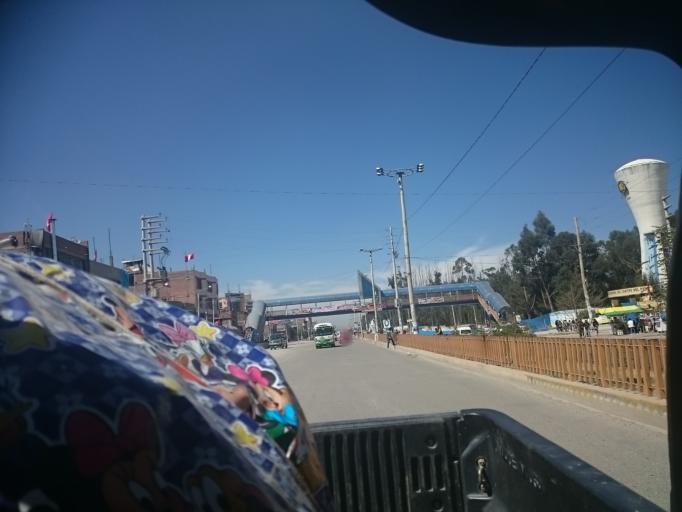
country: PE
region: Junin
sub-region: Provincia de Huancayo
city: Pilcomay
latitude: -12.0301
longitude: -75.2346
